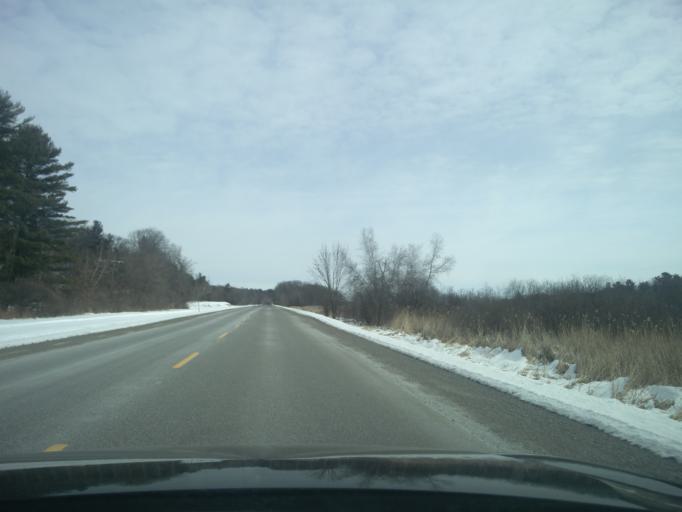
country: US
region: New York
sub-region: Jefferson County
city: Alexandria Bay
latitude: 44.4004
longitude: -75.9169
